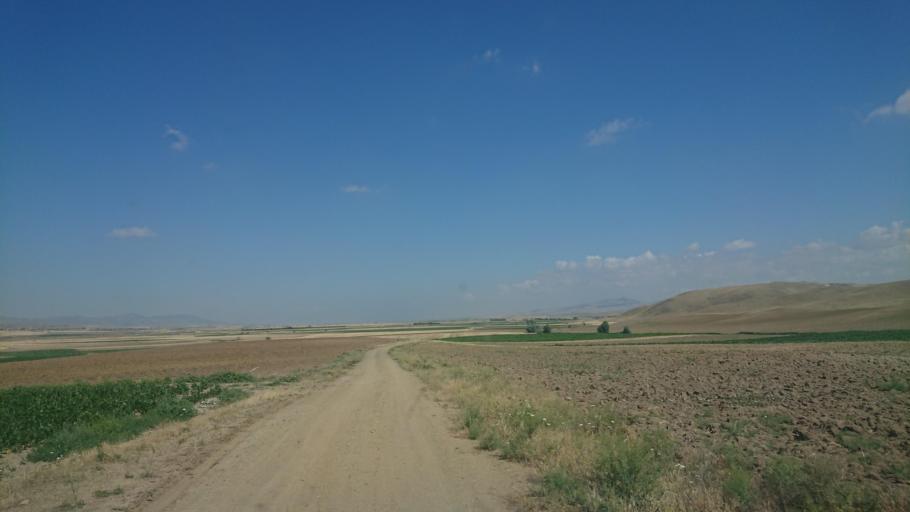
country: TR
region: Aksaray
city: Sariyahsi
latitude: 38.9677
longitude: 33.9216
